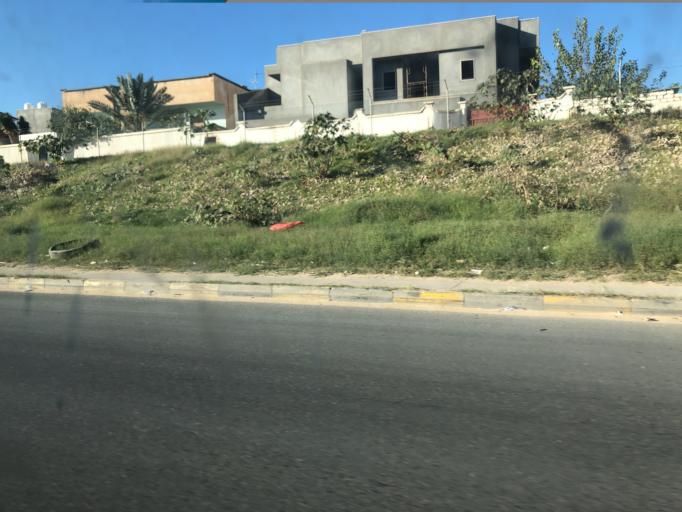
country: LY
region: Tripoli
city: Tripoli
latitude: 32.8689
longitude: 13.2430
